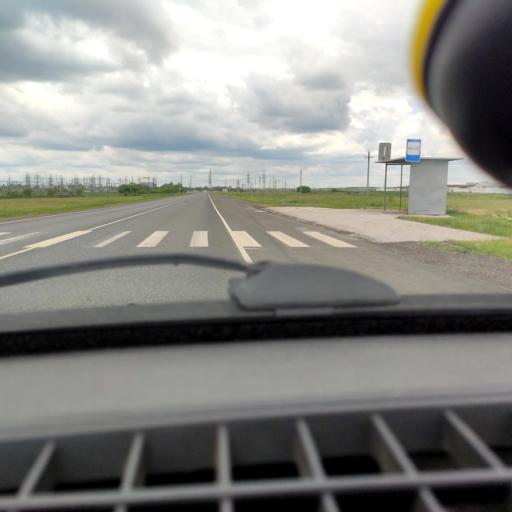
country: RU
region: Samara
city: Povolzhskiy
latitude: 53.6517
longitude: 49.6883
